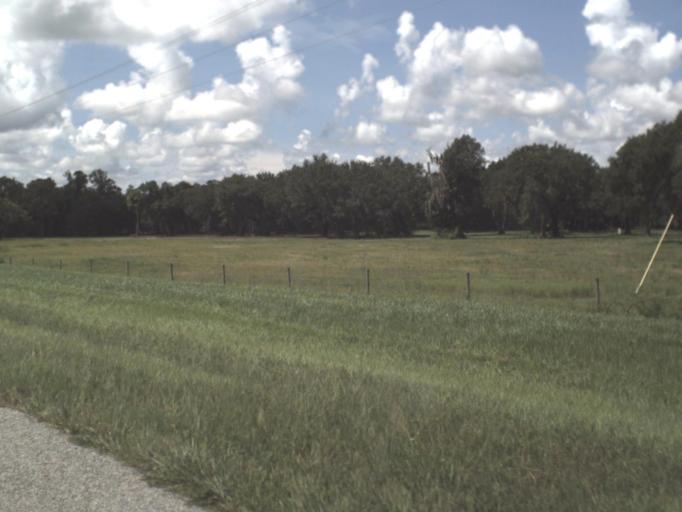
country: US
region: Florida
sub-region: DeSoto County
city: Arcadia
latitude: 27.3203
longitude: -81.8146
